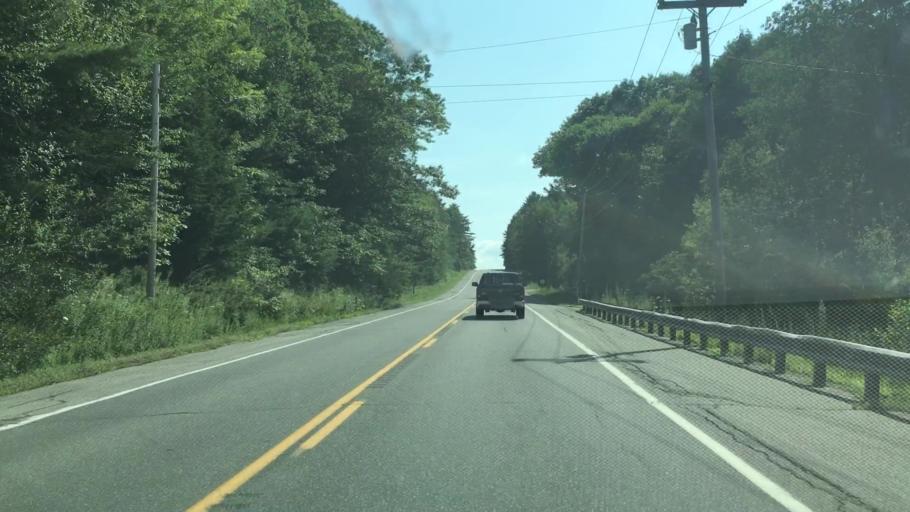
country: US
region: Maine
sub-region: Waldo County
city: Frankfort
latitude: 44.5736
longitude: -68.8620
